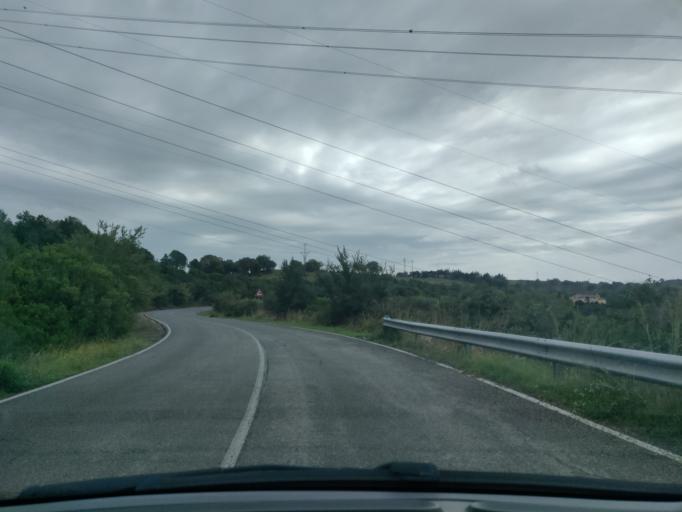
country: IT
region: Latium
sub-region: Citta metropolitana di Roma Capitale
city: Allumiere
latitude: 42.1229
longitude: 11.8630
